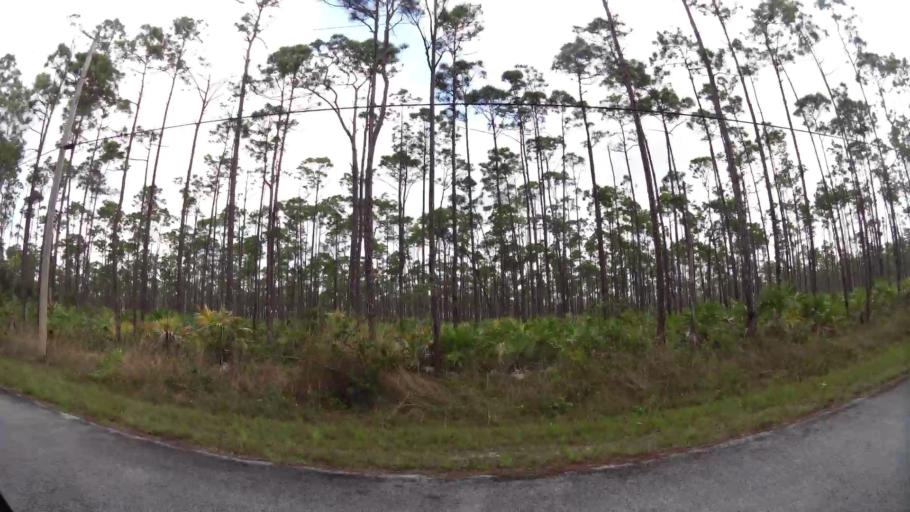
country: BS
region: Freeport
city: Lucaya
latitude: 26.5886
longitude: -78.5466
